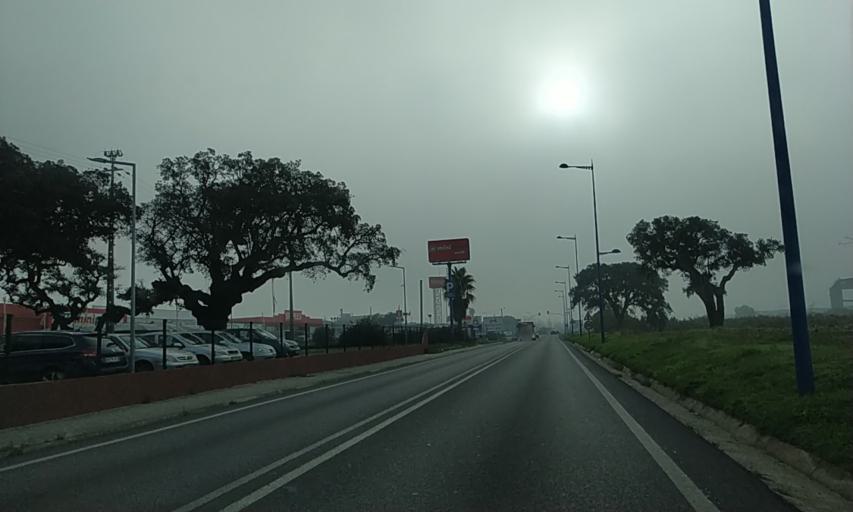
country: PT
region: Setubal
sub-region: Montijo
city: Montijo
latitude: 38.6899
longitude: -8.9474
